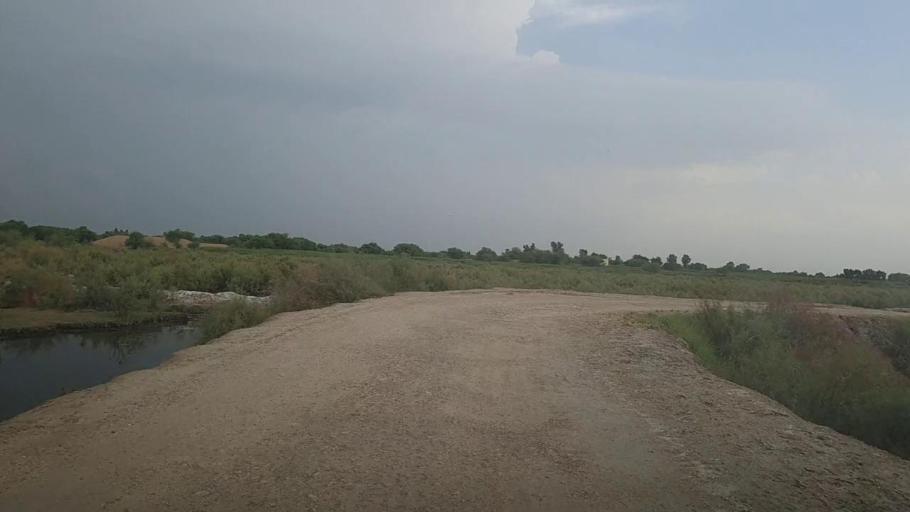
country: PK
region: Sindh
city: Mirpur Mathelo
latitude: 27.9127
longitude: 69.5118
